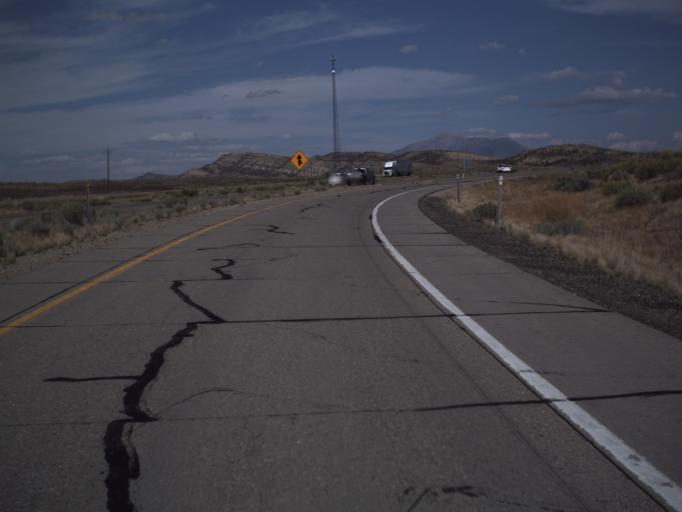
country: US
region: Utah
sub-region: Juab County
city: Nephi
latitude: 39.4376
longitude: -112.0297
